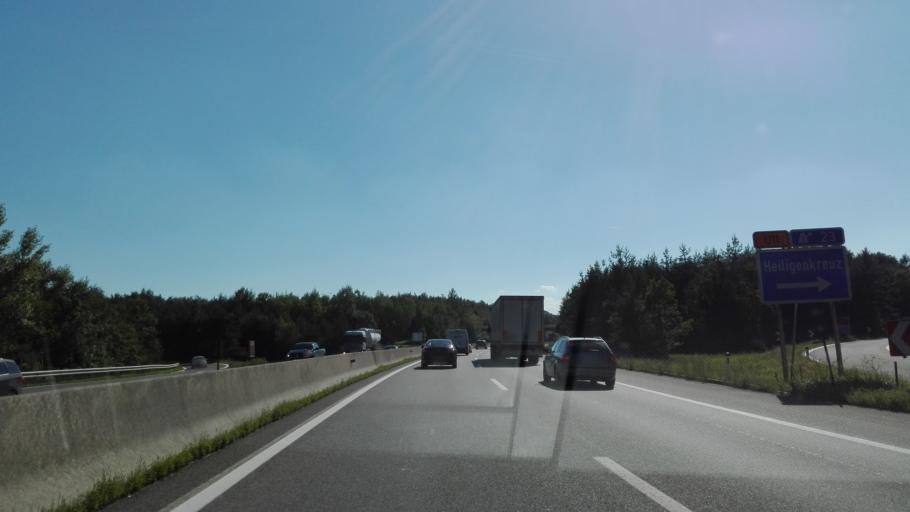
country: AT
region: Lower Austria
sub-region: Politischer Bezirk Baden
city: Heiligenkreuz
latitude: 48.0593
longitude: 16.1603
